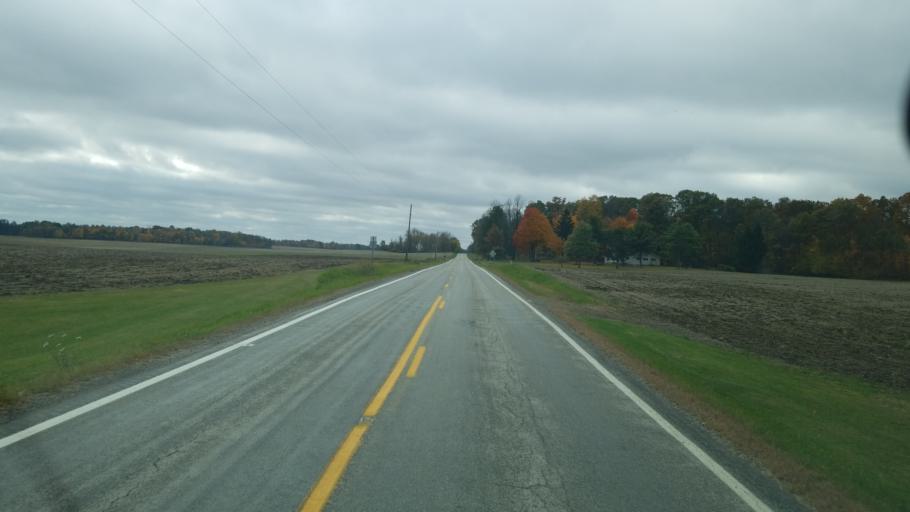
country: US
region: Ohio
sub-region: Richland County
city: Shelby
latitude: 40.8847
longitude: -82.7584
